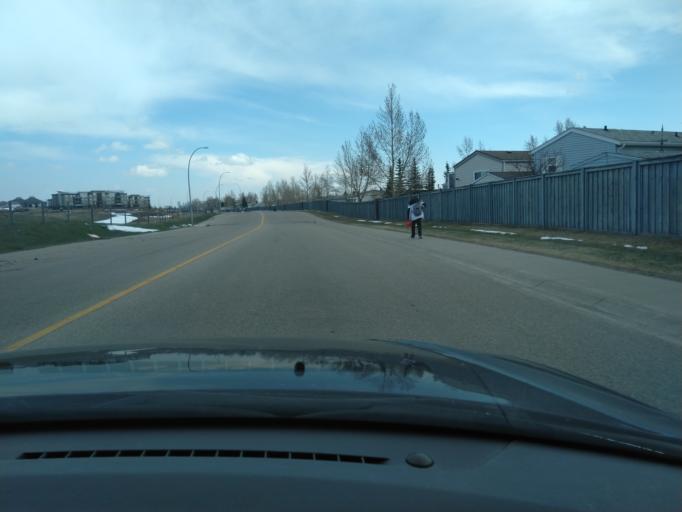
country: CA
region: Alberta
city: Calgary
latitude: 51.1304
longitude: -114.2170
